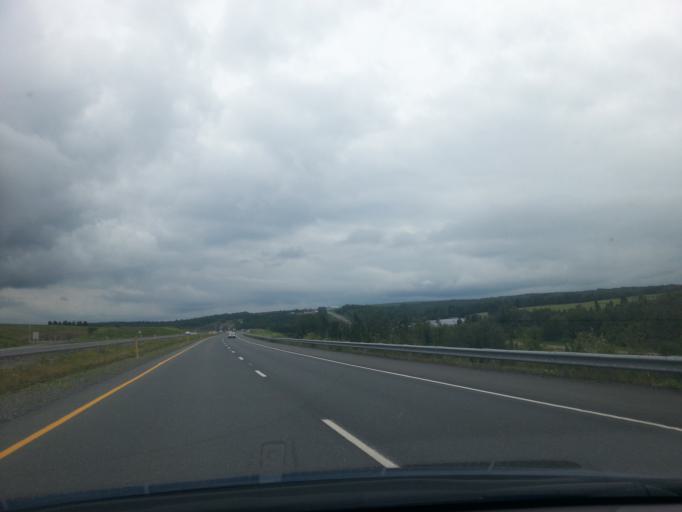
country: US
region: Maine
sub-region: Aroostook County
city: Limestone
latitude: 47.0187
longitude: -67.7588
